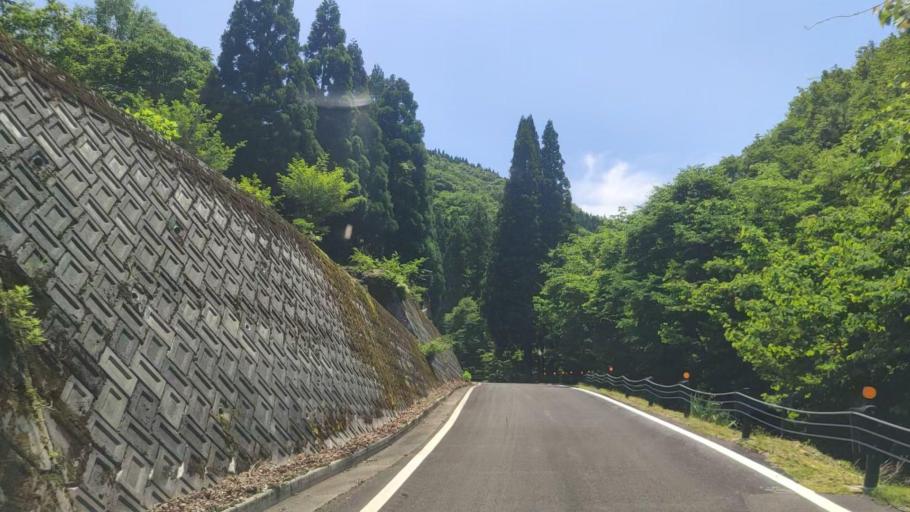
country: JP
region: Tottori
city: Tottori
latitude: 35.3819
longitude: 134.4895
